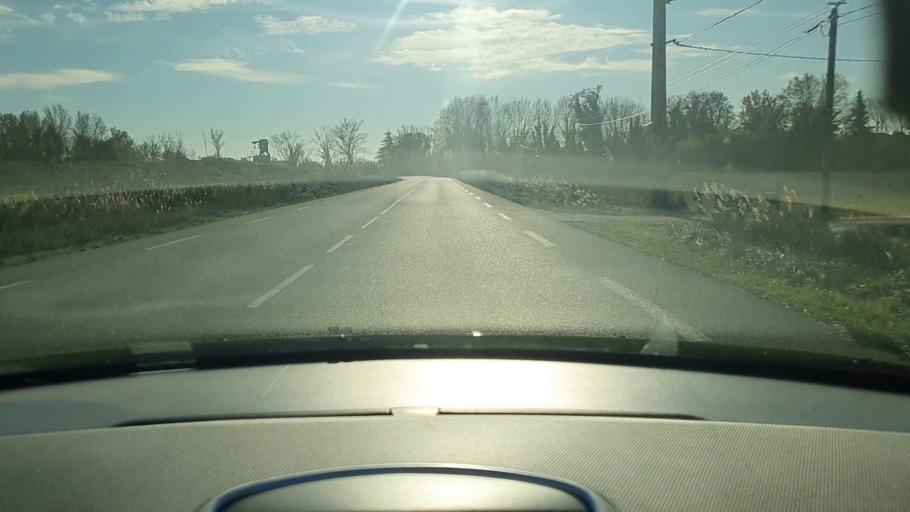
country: FR
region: Languedoc-Roussillon
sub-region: Departement du Gard
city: Fourques
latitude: 43.7265
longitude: 4.6077
